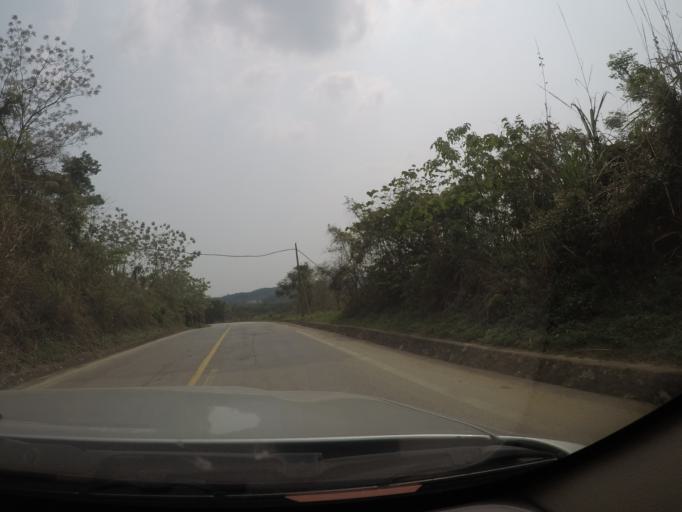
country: VN
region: Thanh Hoa
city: Thi Tran Yen Cat
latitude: 19.4960
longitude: 105.3926
